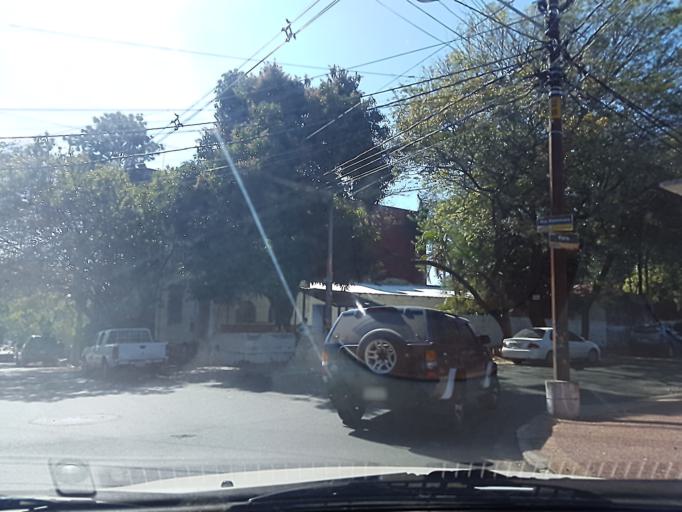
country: PY
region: Asuncion
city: Asuncion
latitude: -25.2842
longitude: -57.6035
